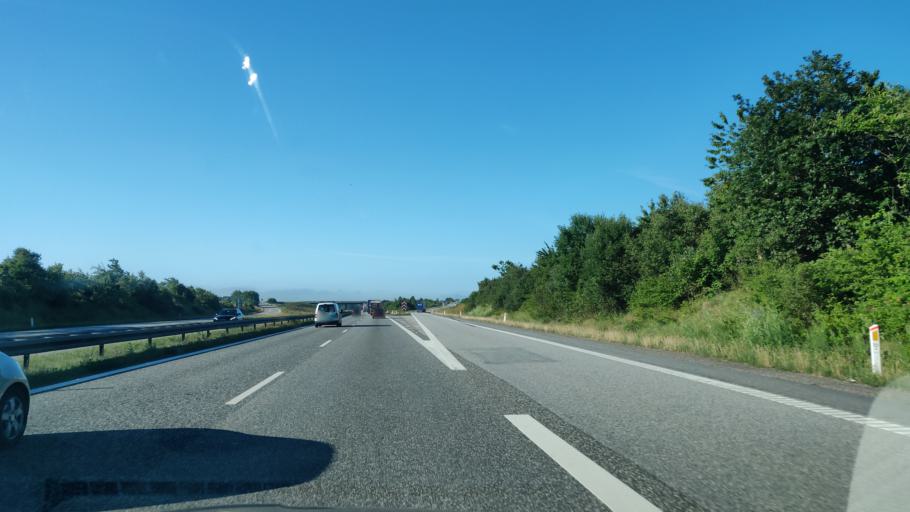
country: DK
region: North Denmark
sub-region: Mariagerfjord Kommune
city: Hobro
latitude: 56.6718
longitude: 9.7331
